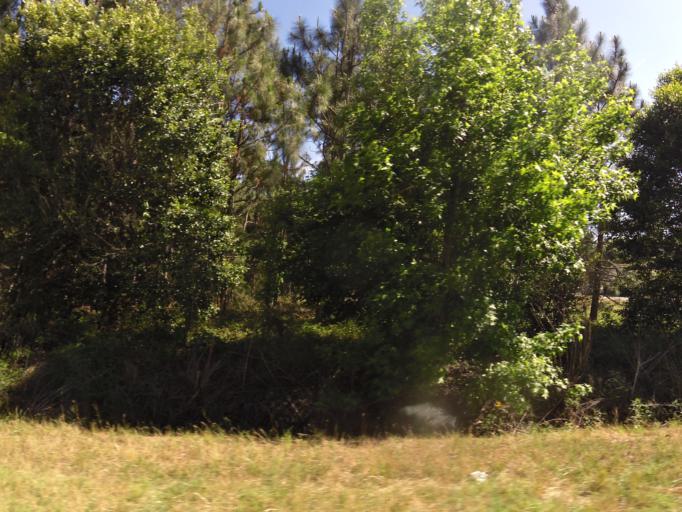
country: US
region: South Carolina
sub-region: Barnwell County
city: Blackville
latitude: 33.3491
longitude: -81.2269
